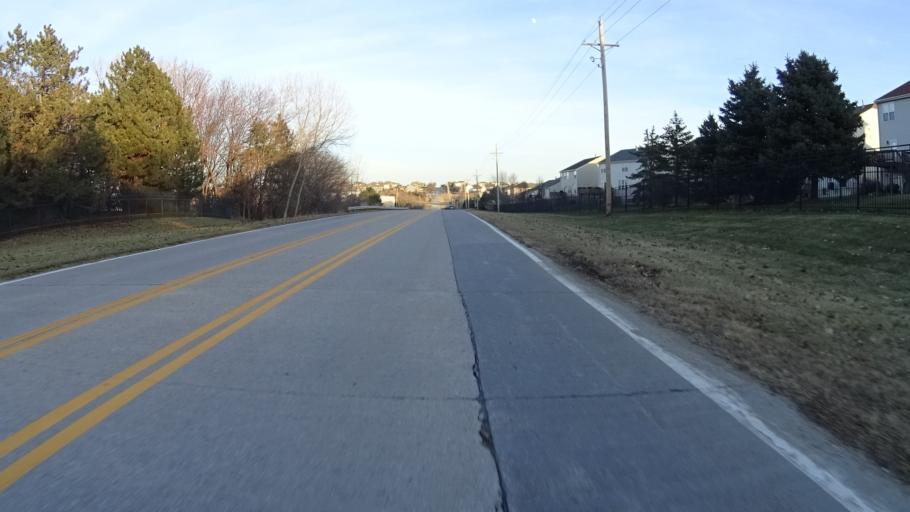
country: US
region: Nebraska
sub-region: Sarpy County
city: Papillion
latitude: 41.1326
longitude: -96.0712
